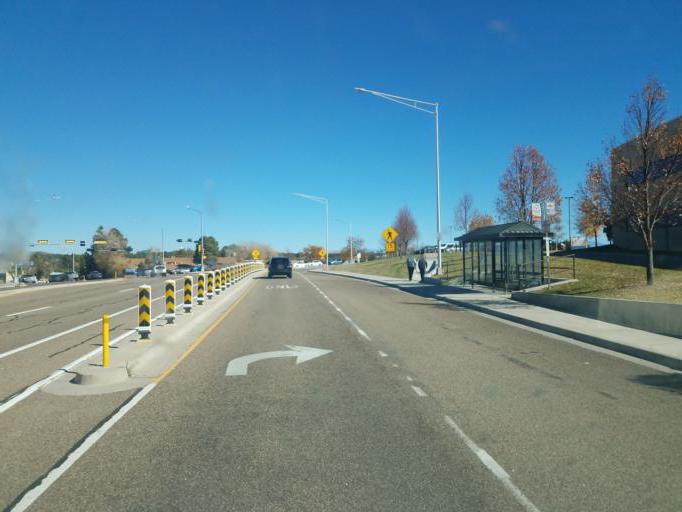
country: US
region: New Mexico
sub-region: Los Alamos County
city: Los Alamos
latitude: 35.8824
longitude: -106.3197
